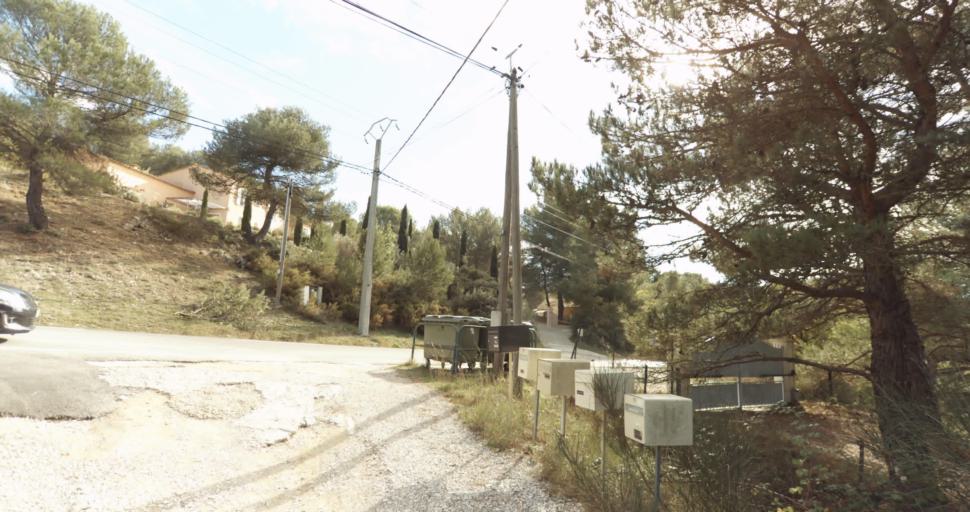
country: FR
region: Provence-Alpes-Cote d'Azur
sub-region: Departement des Bouches-du-Rhone
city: Venelles
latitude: 43.6072
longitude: 5.4921
